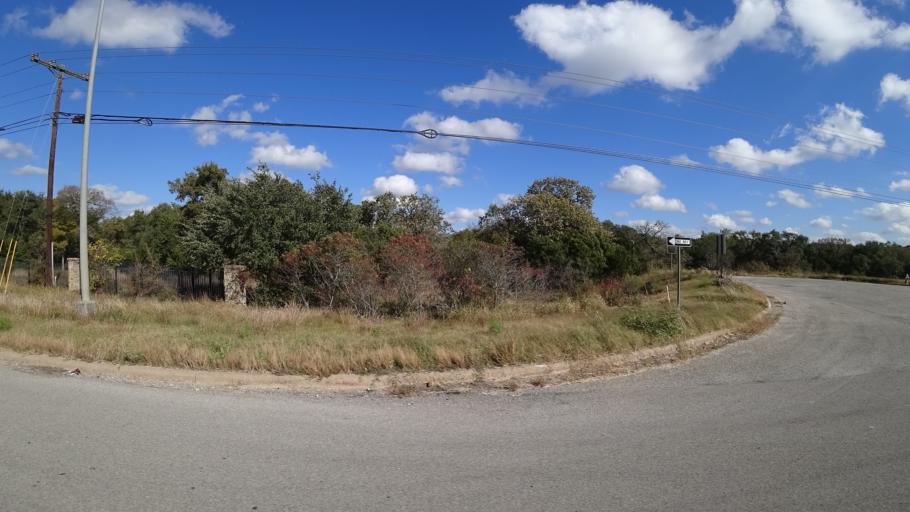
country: US
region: Texas
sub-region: Travis County
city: Shady Hollow
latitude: 30.1875
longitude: -97.9131
